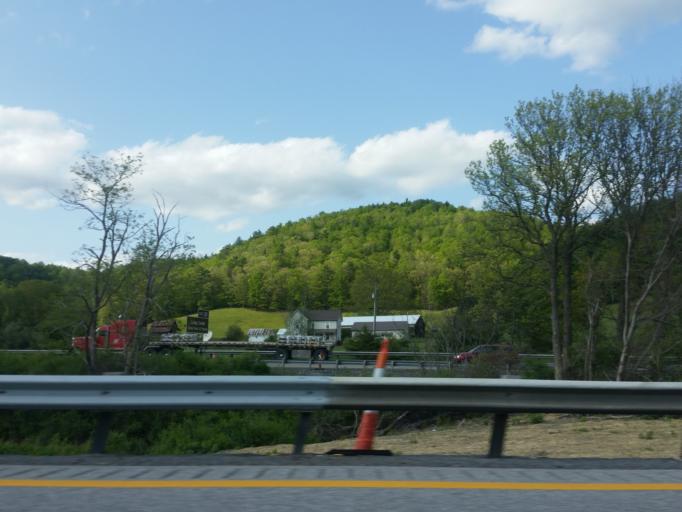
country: US
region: West Virginia
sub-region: Mercer County
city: Athens
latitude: 37.4923
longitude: -81.0916
